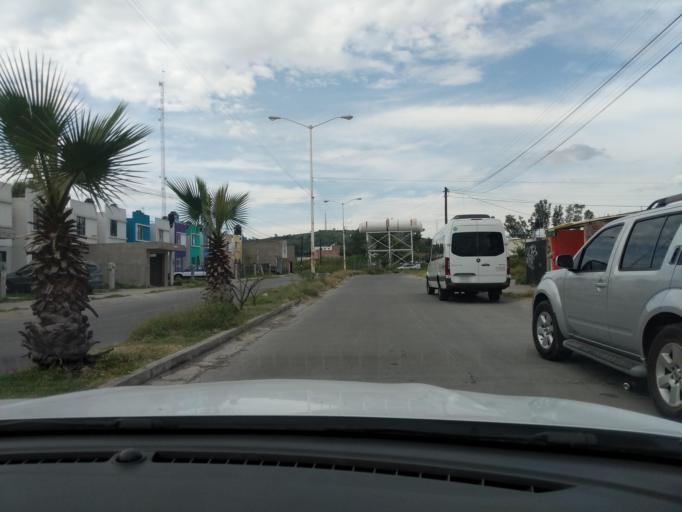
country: MX
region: Jalisco
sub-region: El Salto
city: Galaxia Bonito Jalisco
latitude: 20.5089
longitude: -103.1910
